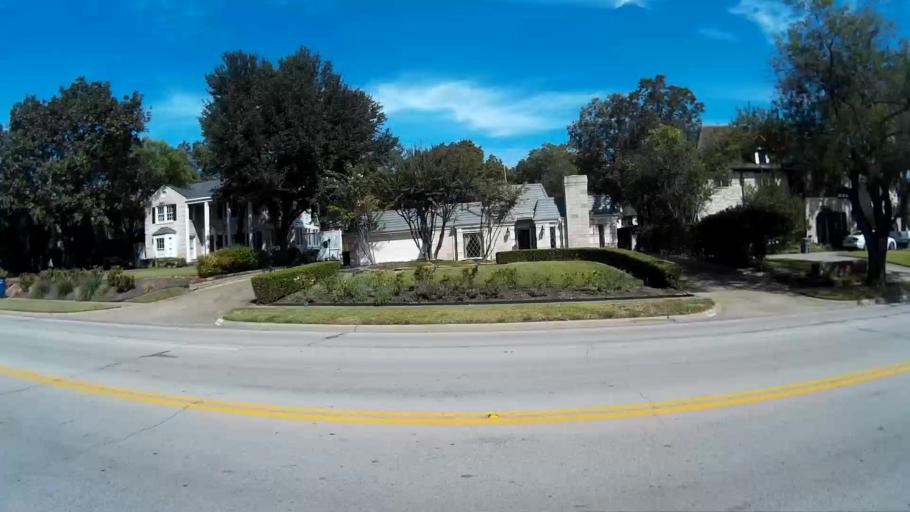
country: US
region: Texas
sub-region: Dallas County
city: Highland Park
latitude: 32.8163
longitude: -96.7452
